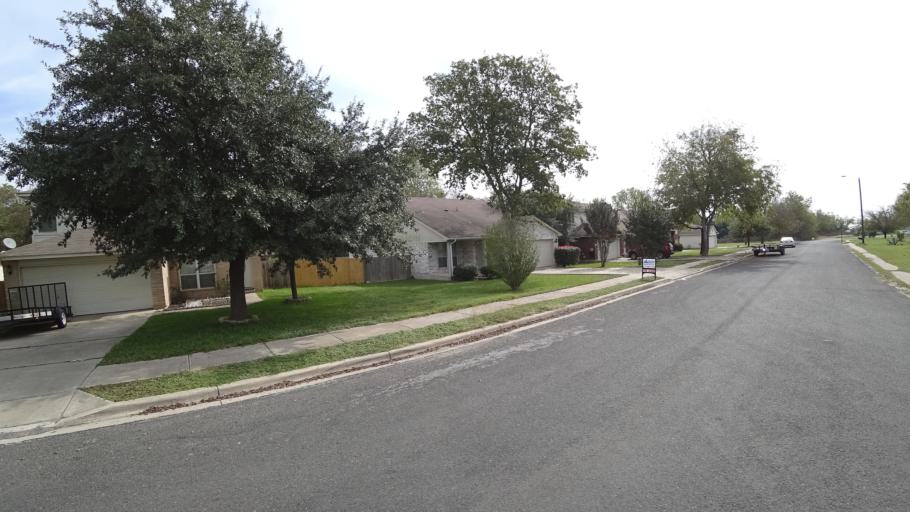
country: US
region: Texas
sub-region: Travis County
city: Windemere
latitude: 30.4430
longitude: -97.6597
